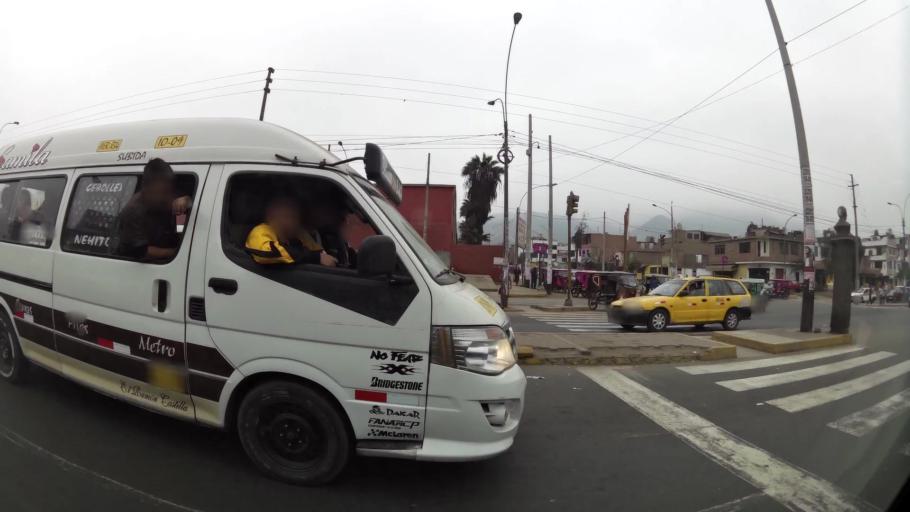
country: PE
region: Lima
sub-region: Lima
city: Urb. Santo Domingo
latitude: -11.9171
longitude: -77.0413
